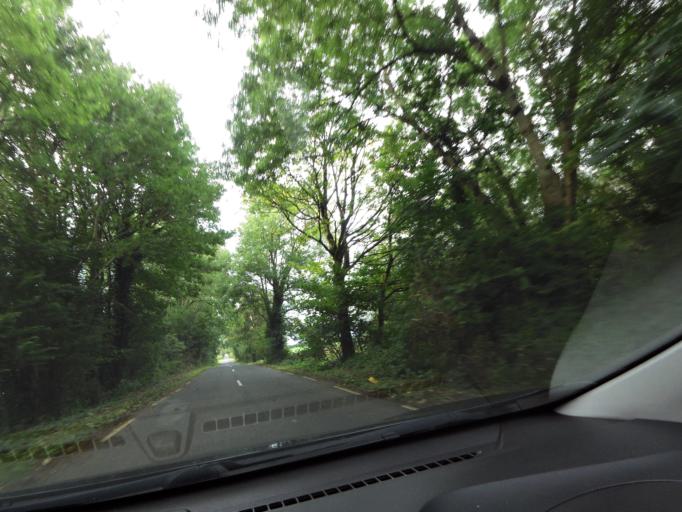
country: IE
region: Leinster
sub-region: Uibh Fhaili
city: Ferbane
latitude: 53.1986
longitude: -7.7805
